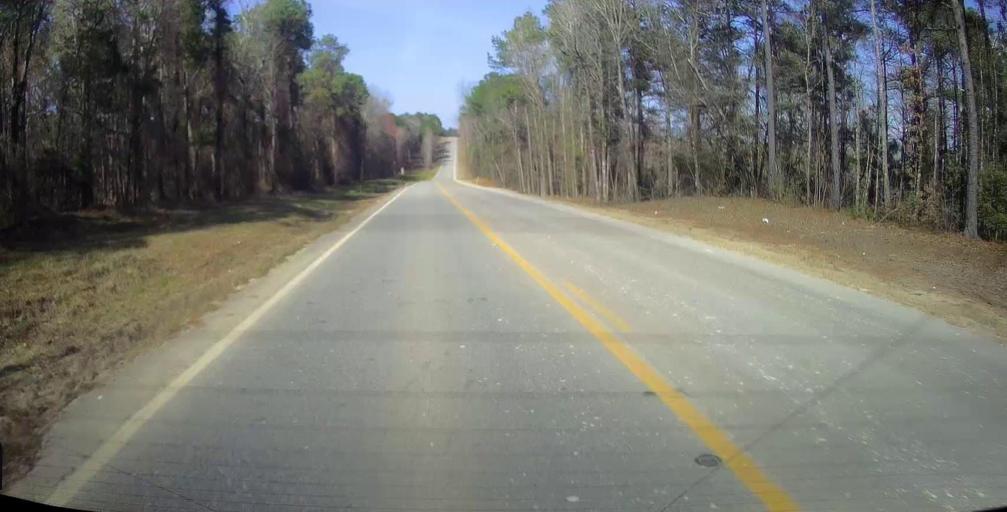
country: US
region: Georgia
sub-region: Wilkinson County
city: Gordon
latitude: 32.7979
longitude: -83.3303
